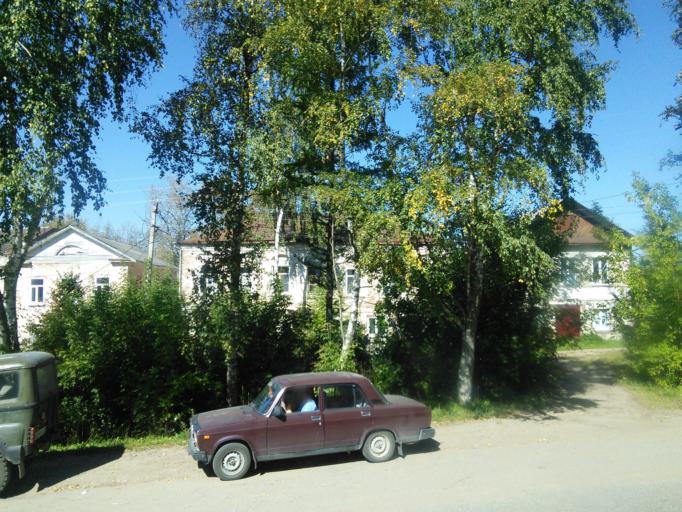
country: RU
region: Tverskaya
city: Kashin
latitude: 57.3624
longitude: 37.6090
